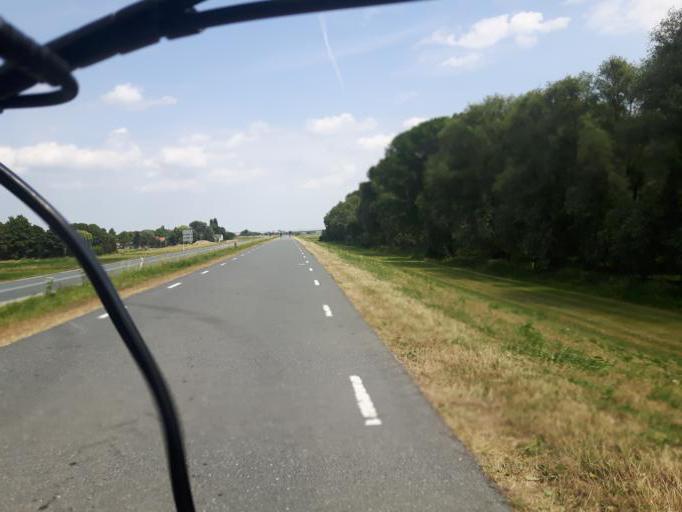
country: NL
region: Gelderland
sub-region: Gemeente Zaltbommel
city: Zaltbommel
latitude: 51.8201
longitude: 5.2298
